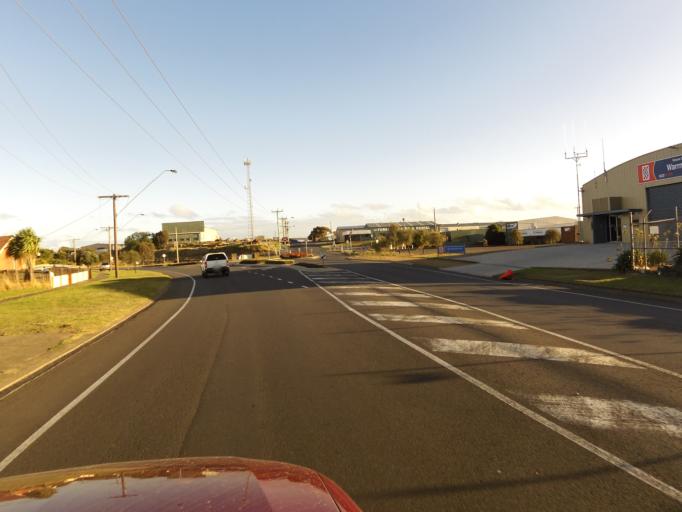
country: AU
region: Victoria
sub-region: Warrnambool
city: Warrnambool
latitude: -38.3669
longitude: 142.4592
